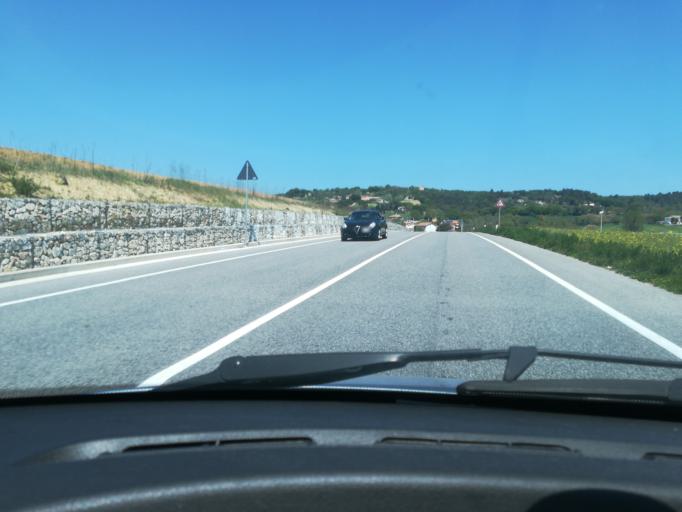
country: IT
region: The Marches
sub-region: Provincia di Ancona
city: Villa Musone
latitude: 43.4551
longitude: 13.5809
